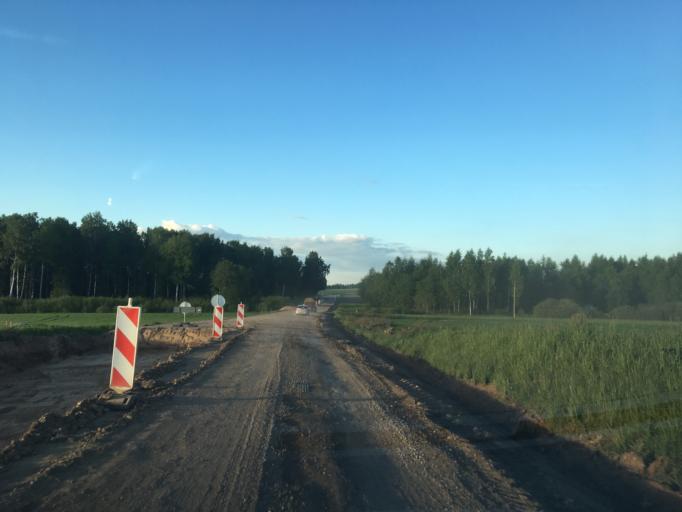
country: EE
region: Tartu
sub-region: UElenurme vald
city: Ulenurme
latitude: 58.2406
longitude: 26.6621
